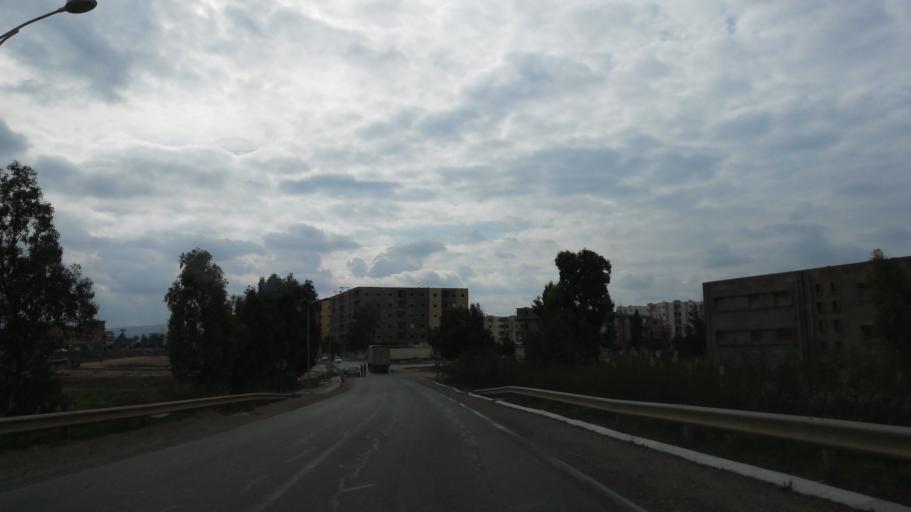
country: DZ
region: Oran
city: Sidi ech Chahmi
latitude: 35.5590
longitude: -0.4479
